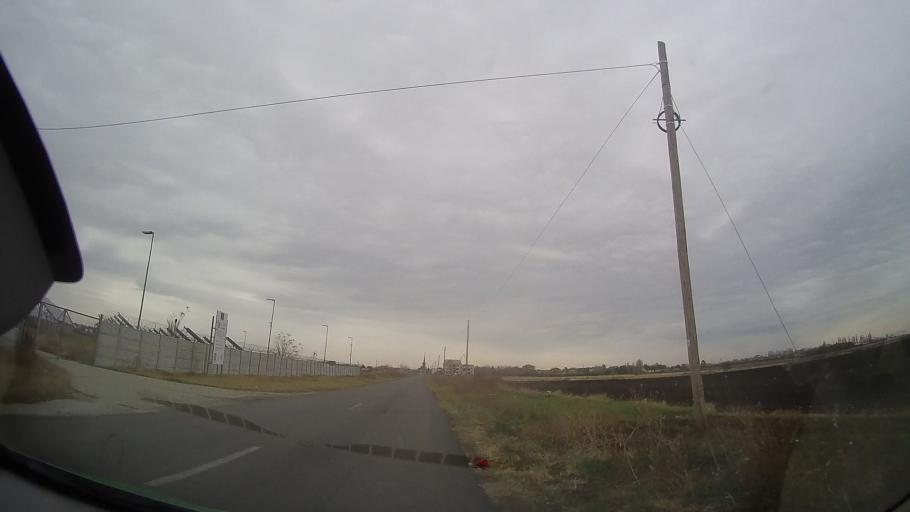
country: RO
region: Prahova
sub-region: Oras Mizil
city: Mizil
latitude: 45.0058
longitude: 26.4258
